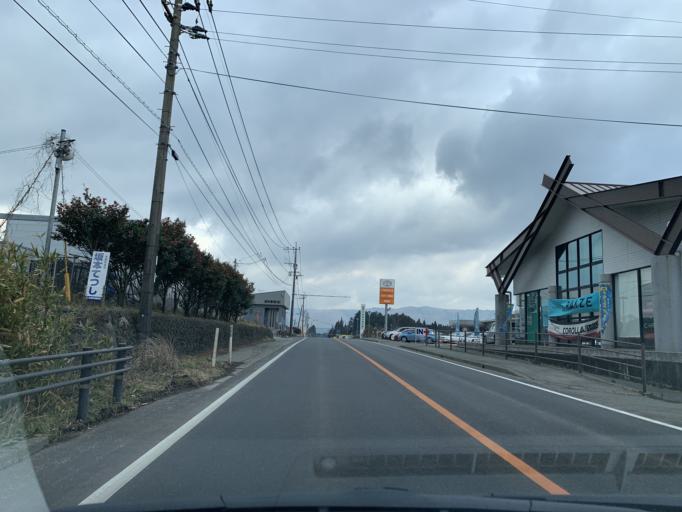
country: JP
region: Kumamoto
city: Aso
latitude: 32.9346
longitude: 131.0610
